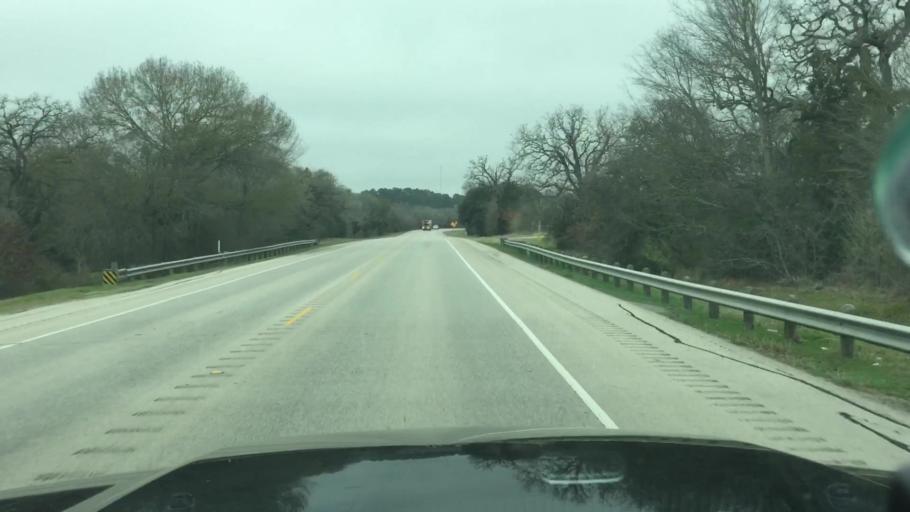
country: US
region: Texas
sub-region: Fayette County
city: La Grange
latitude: 30.0298
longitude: -96.9064
